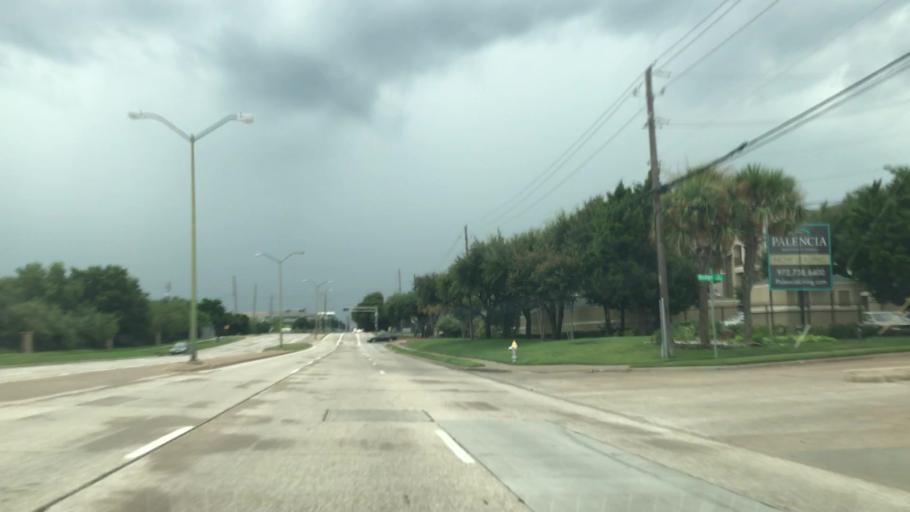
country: US
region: Texas
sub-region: Dallas County
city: Richardson
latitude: 32.9946
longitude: -96.7679
